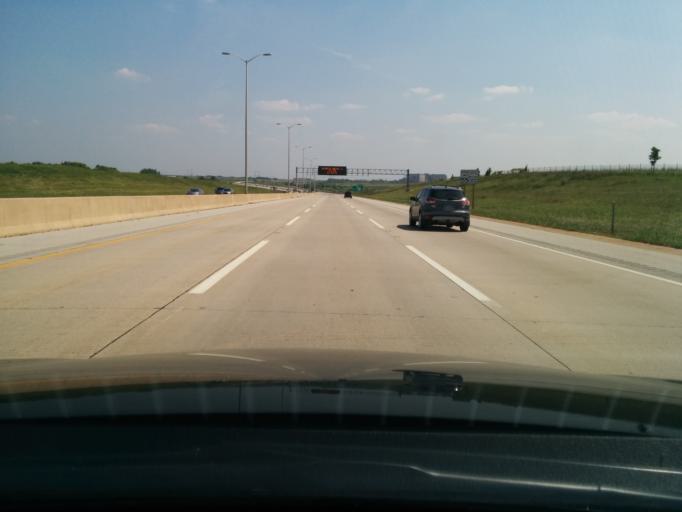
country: US
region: Illinois
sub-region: Will County
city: New Lenox
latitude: 41.5627
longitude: -87.9905
